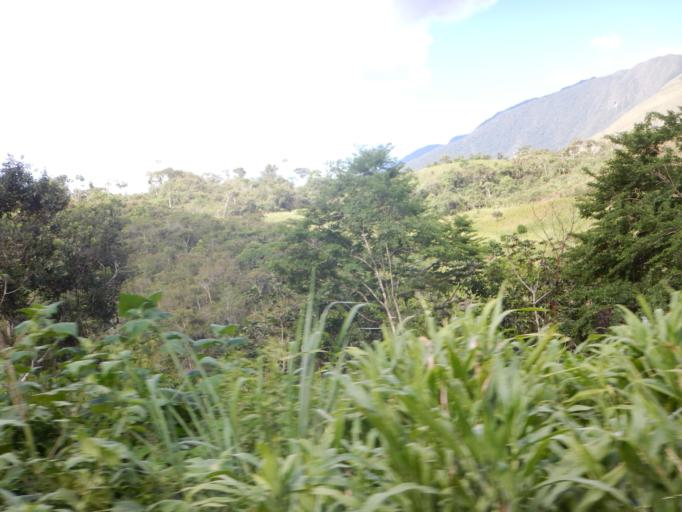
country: BO
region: La Paz
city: Coroico
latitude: -16.1610
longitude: -67.7317
